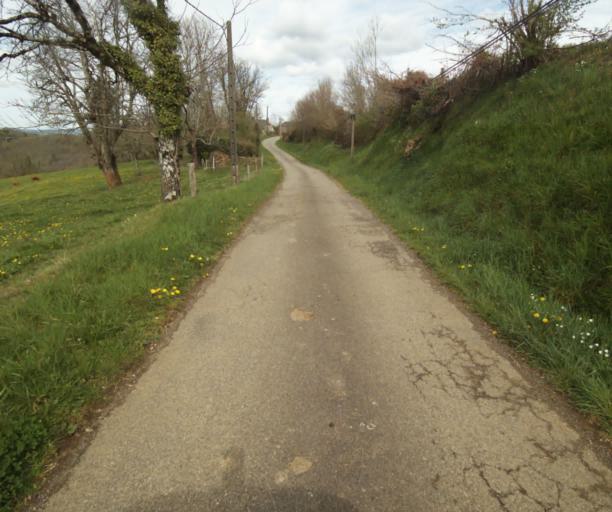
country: FR
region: Limousin
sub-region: Departement de la Correze
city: Laguenne
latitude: 45.2231
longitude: 1.8479
